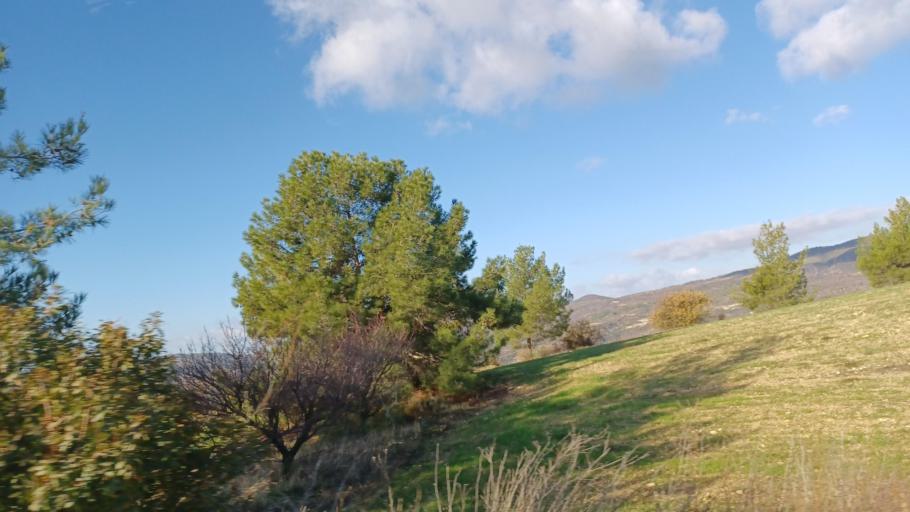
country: CY
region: Limassol
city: Pachna
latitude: 34.8470
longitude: 32.7392
